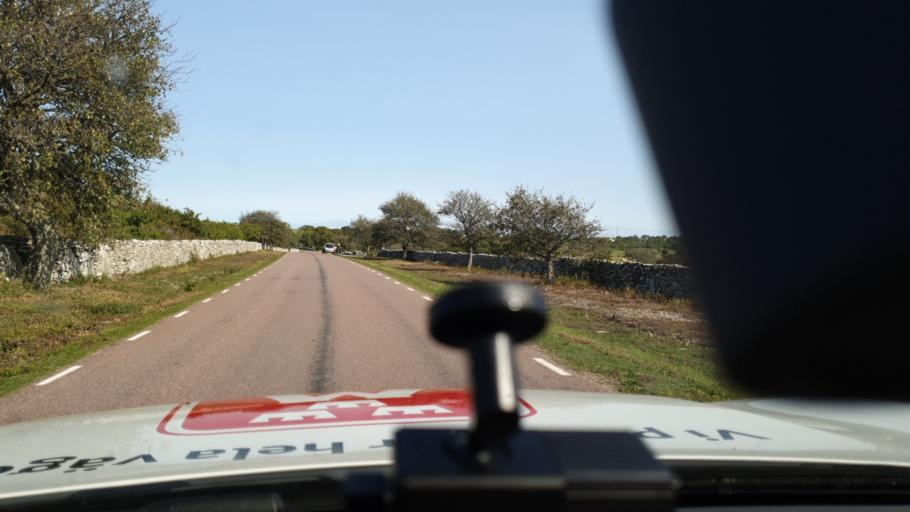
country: SE
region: Gotland
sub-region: Gotland
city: Hemse
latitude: 56.9171
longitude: 18.1540
